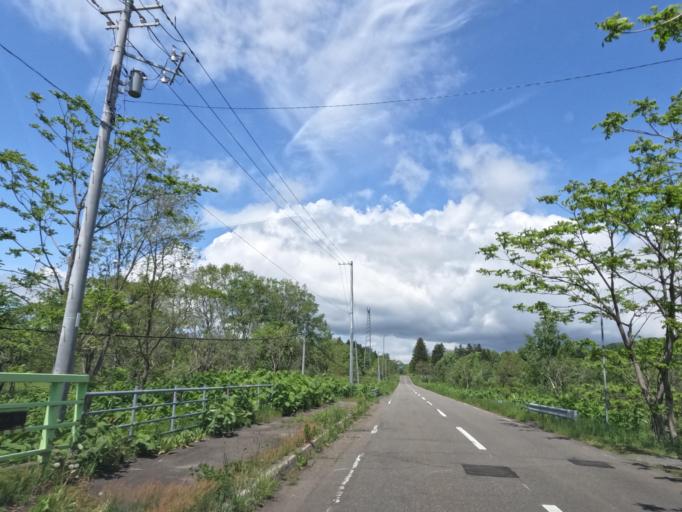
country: JP
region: Hokkaido
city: Tobetsu
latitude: 43.4056
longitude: 141.5824
